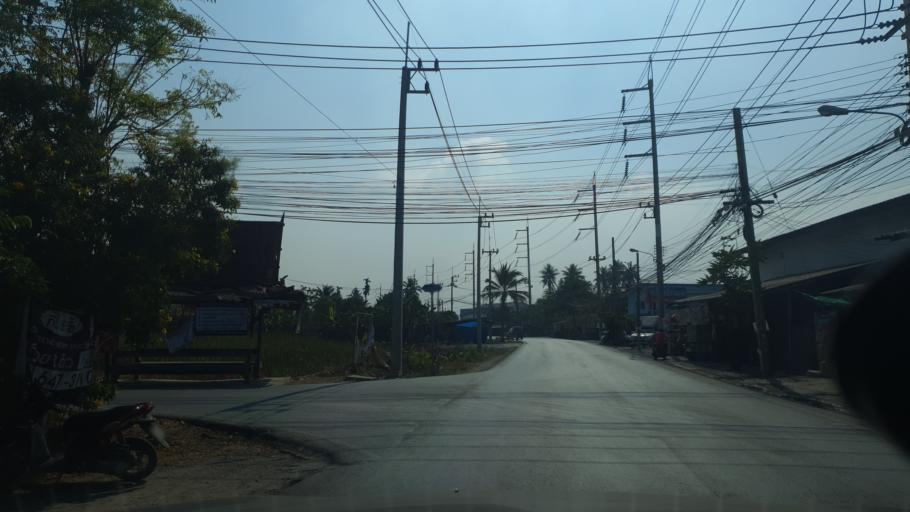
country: TH
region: Nakhon Pathom
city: Salaya
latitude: 13.7764
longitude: 100.2764
